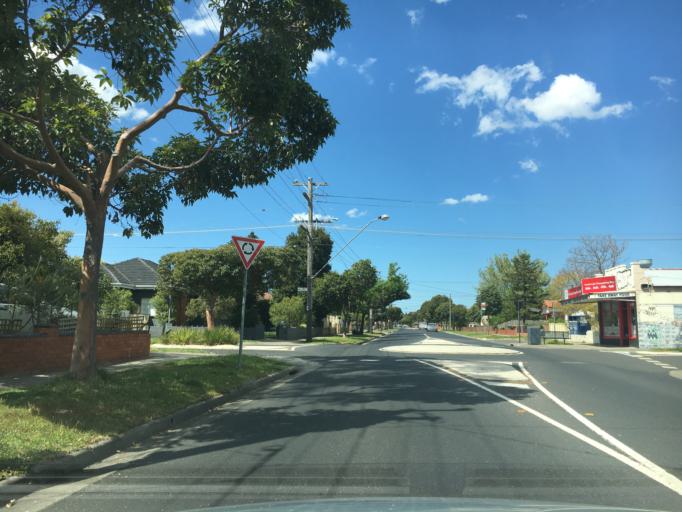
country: AU
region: Victoria
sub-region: Monash
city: Chadstone
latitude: -37.9030
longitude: 145.1007
